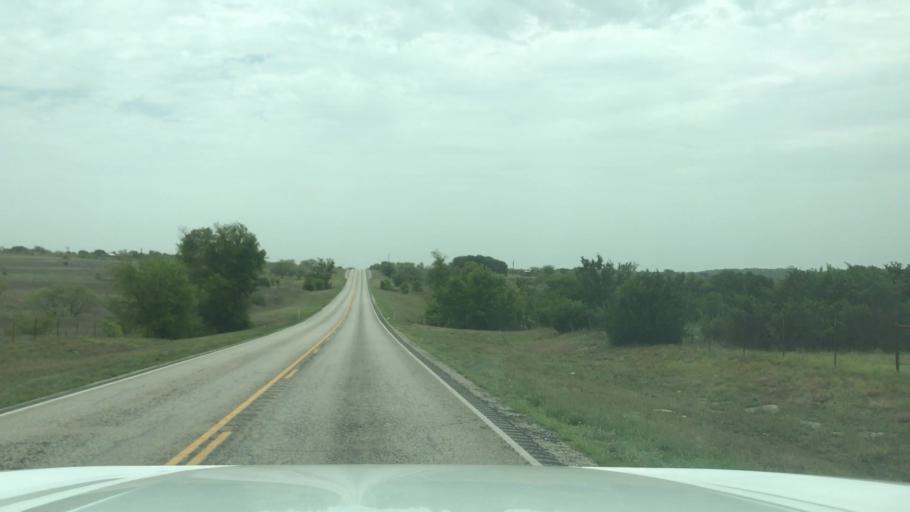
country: US
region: Texas
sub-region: Hamilton County
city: Hico
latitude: 32.0526
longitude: -98.1694
